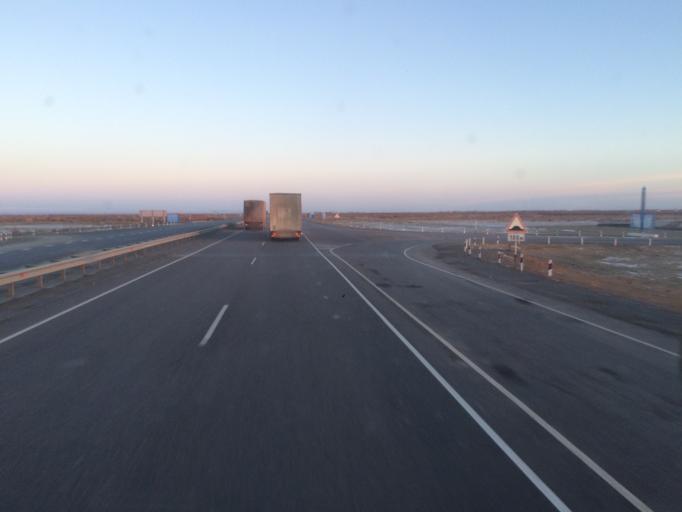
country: KZ
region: Qyzylorda
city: Zhangaqorghan
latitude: 44.1024
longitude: 67.0546
